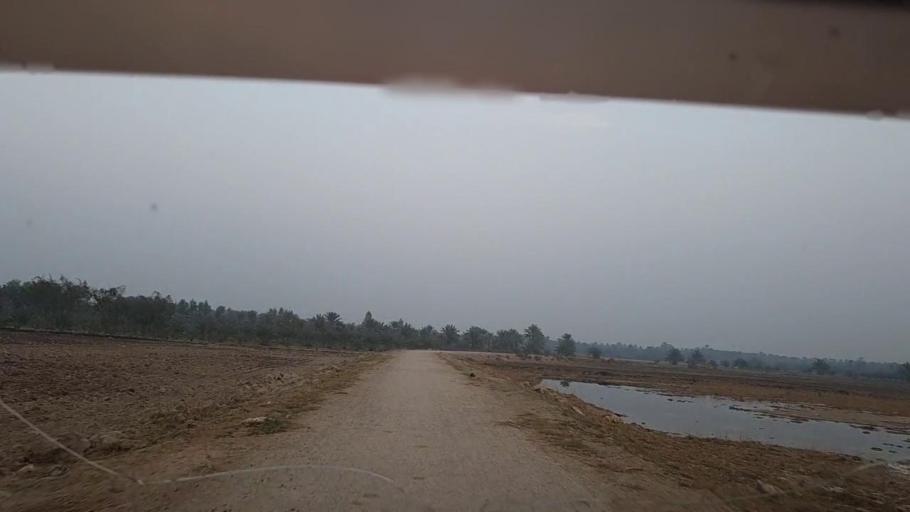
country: PK
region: Sindh
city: Khairpur
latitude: 27.5778
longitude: 68.7321
